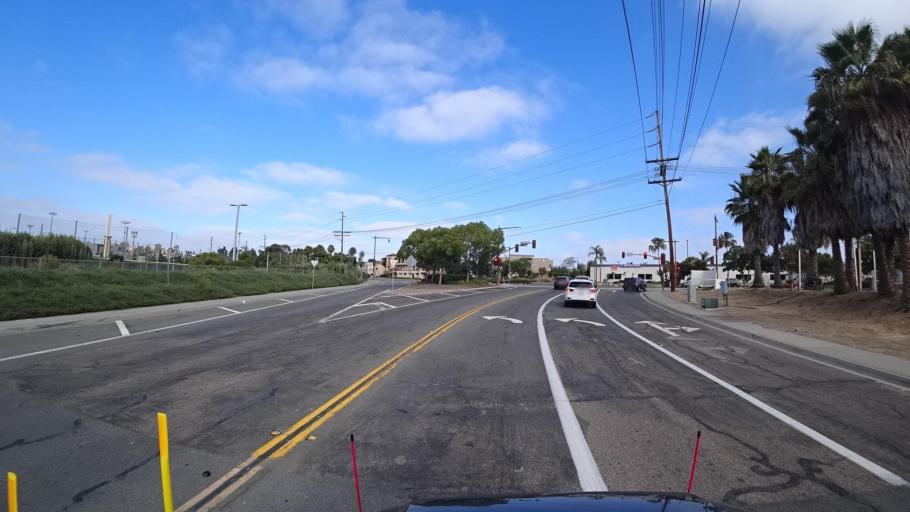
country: US
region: California
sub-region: San Diego County
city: Lake San Marcos
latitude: 33.1307
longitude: -117.2008
